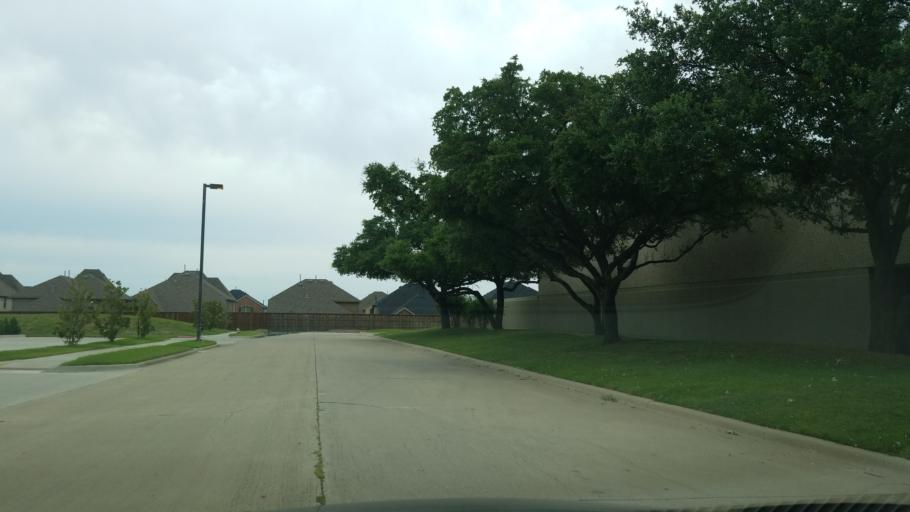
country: US
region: Texas
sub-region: Dallas County
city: Coppell
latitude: 32.8976
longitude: -96.9893
